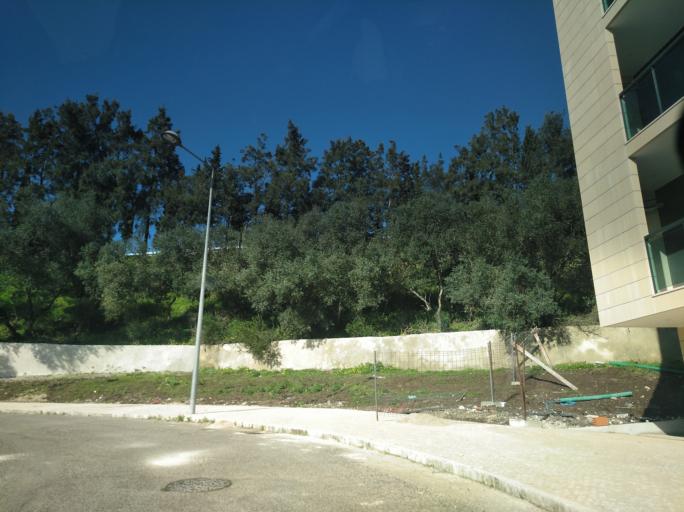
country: PT
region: Lisbon
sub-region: Odivelas
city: Famoes
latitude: 38.7912
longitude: -9.2071
